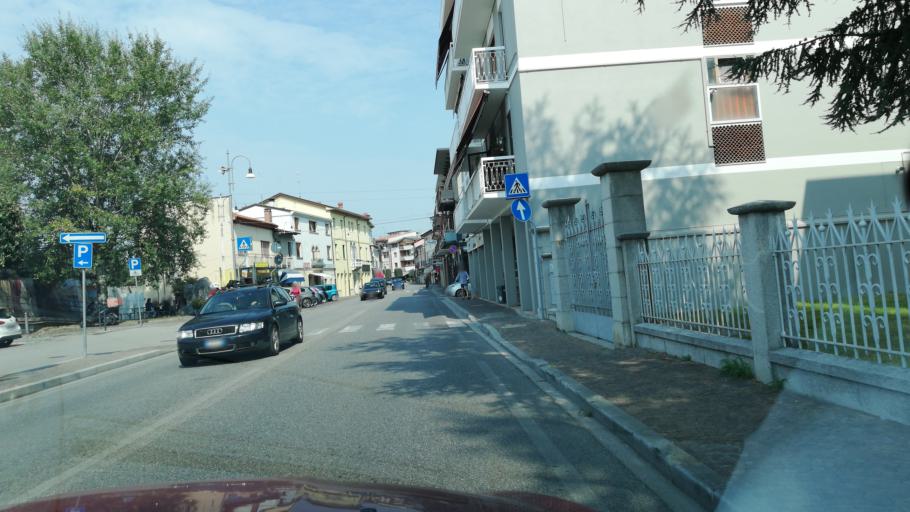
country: IT
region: Veneto
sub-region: Provincia di Venezia
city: San Michele al Tagliamento
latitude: 45.7736
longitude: 12.9970
